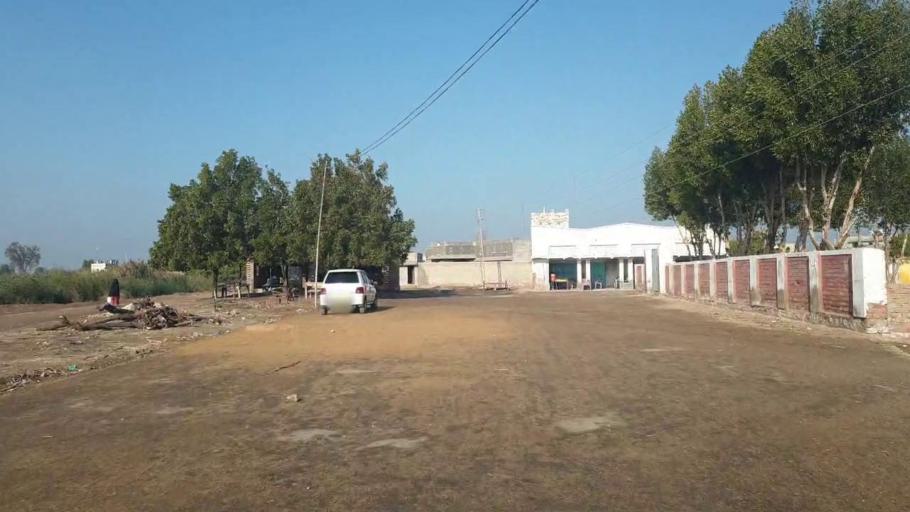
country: PK
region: Sindh
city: Shahdadpur
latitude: 25.9054
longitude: 68.5947
